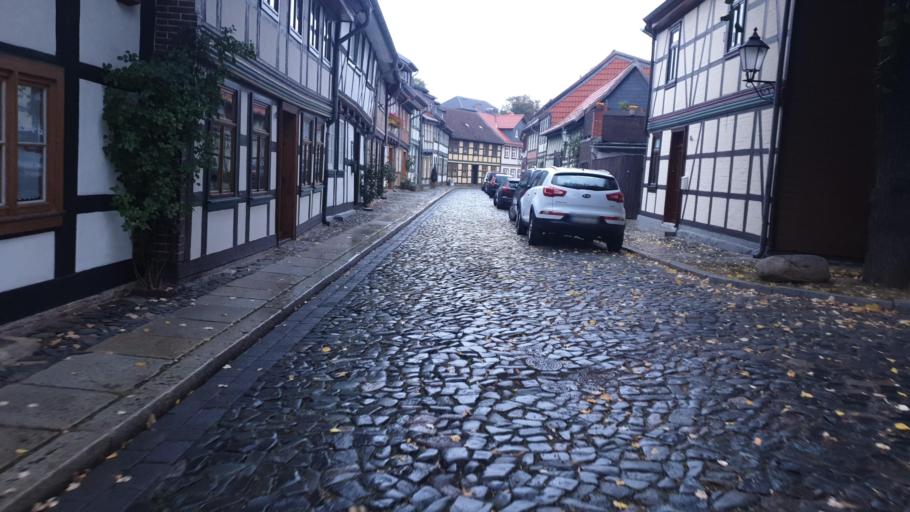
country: DE
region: Saxony-Anhalt
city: Wernigerode
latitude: 51.8339
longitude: 10.7818
